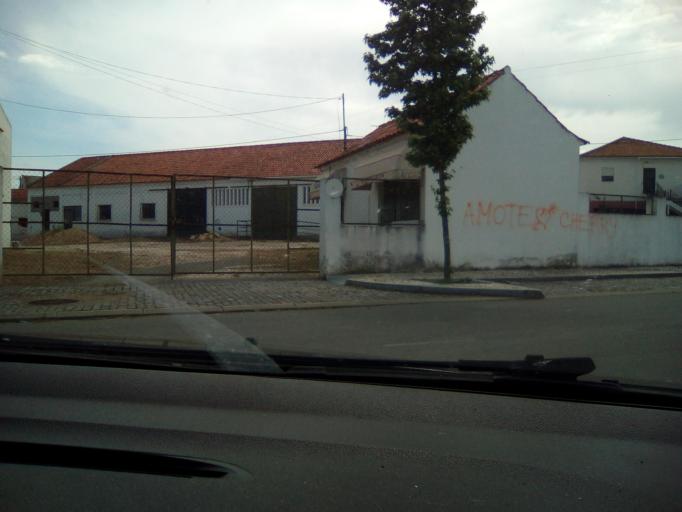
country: PT
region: Portalegre
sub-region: Avis
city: Avis
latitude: 39.0527
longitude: -7.8876
